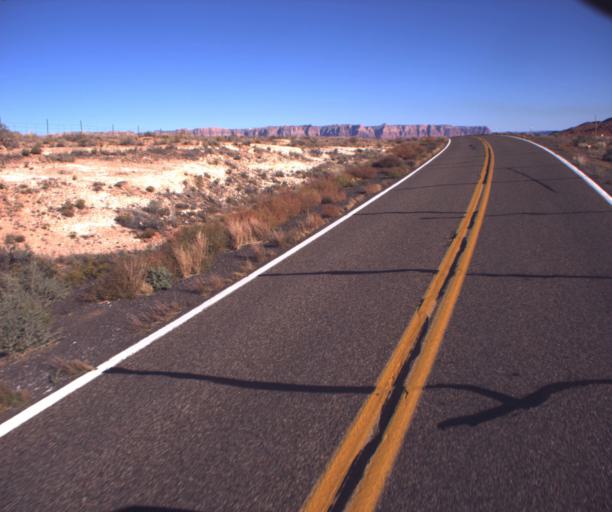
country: US
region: Arizona
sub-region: Coconino County
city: LeChee
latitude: 36.6608
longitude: -111.6504
